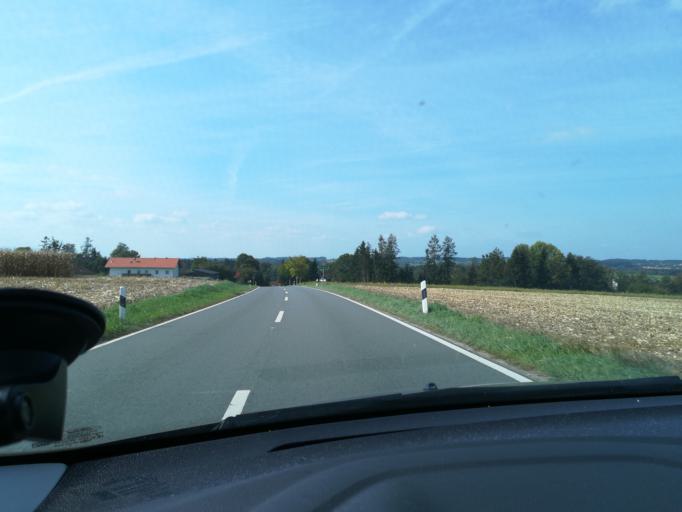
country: DE
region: Bavaria
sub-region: Upper Bavaria
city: Pfaffing
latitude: 48.0243
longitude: 12.1018
